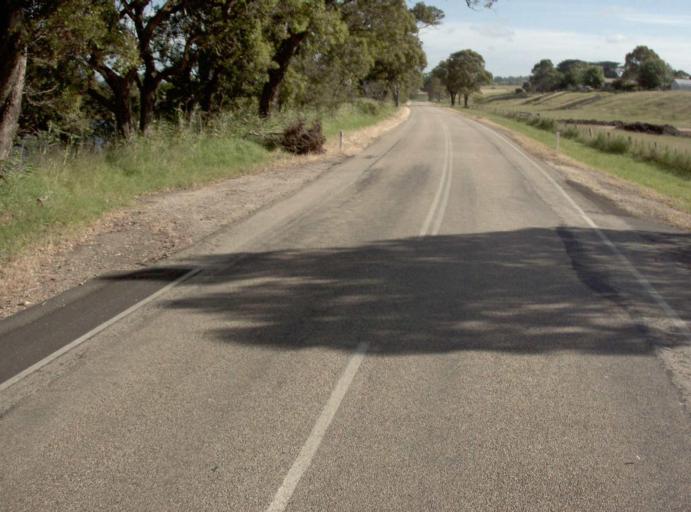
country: AU
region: Victoria
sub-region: East Gippsland
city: Lakes Entrance
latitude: -37.8386
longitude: 147.8607
